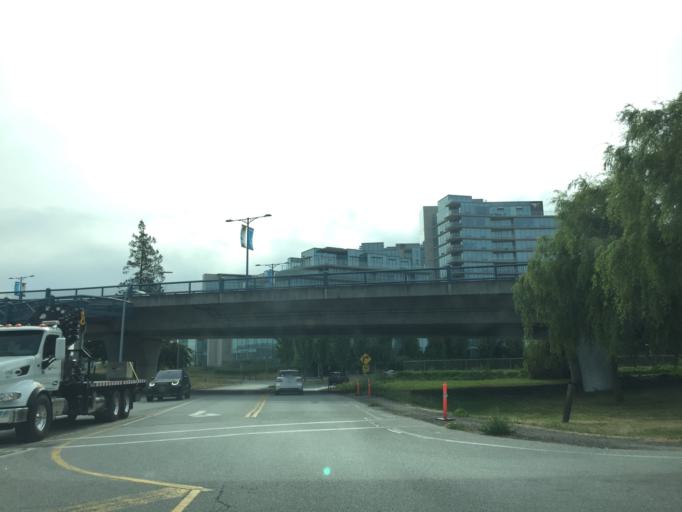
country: CA
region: British Columbia
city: Richmond
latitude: 49.1738
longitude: -123.1591
